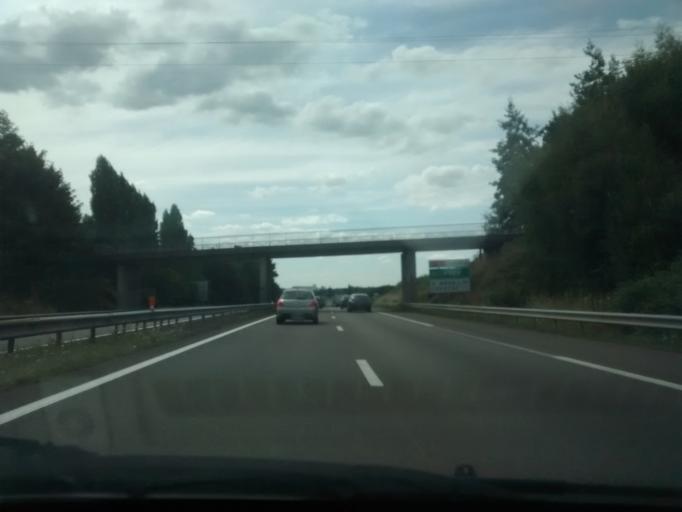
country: FR
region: Brittany
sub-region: Departement d'Ille-et-Vilaine
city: Montauban-de-Bretagne
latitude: 48.2081
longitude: -2.0649
